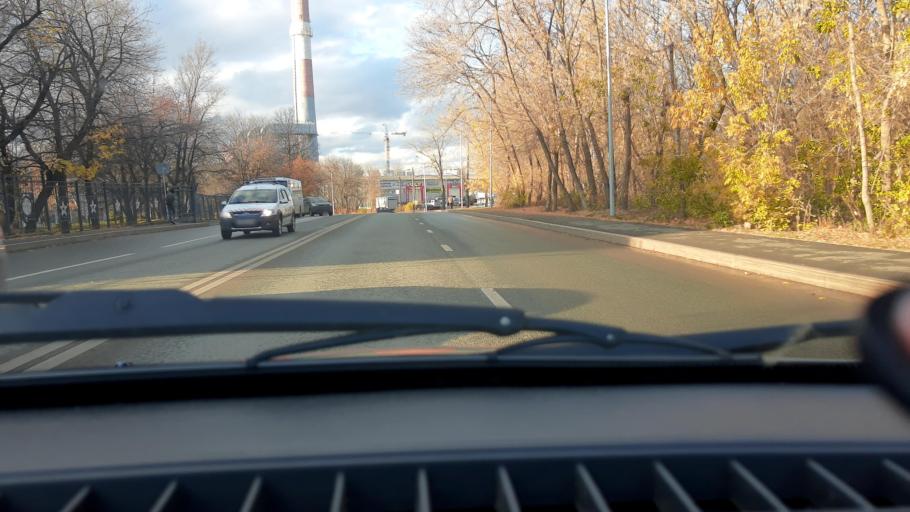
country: RU
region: Bashkortostan
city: Ufa
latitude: 54.7119
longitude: 56.0083
